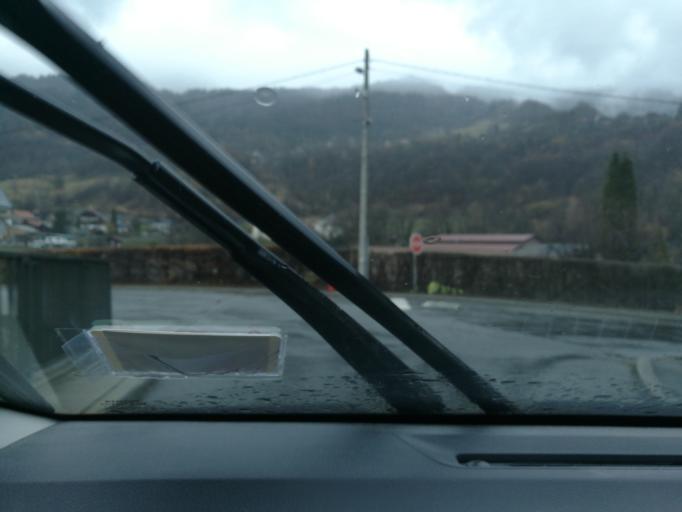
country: FR
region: Rhone-Alpes
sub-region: Departement de la Haute-Savoie
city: Saint-Gervais-les-Bains
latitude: 45.9275
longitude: 6.7264
